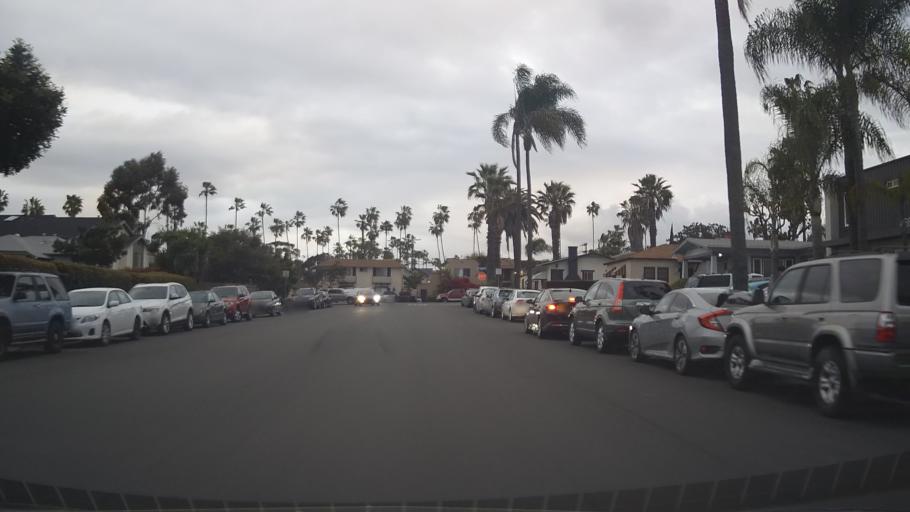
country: US
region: California
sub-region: San Diego County
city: San Diego
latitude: 32.7620
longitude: -117.1414
